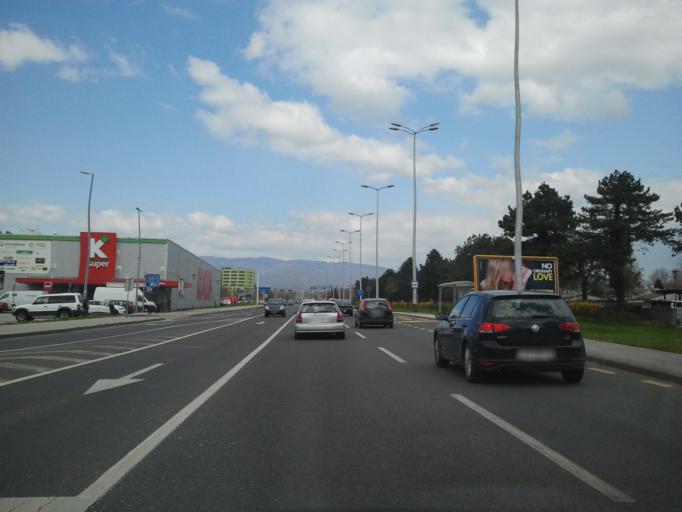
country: HR
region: Grad Zagreb
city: Novi Zagreb
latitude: 45.7687
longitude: 16.0056
